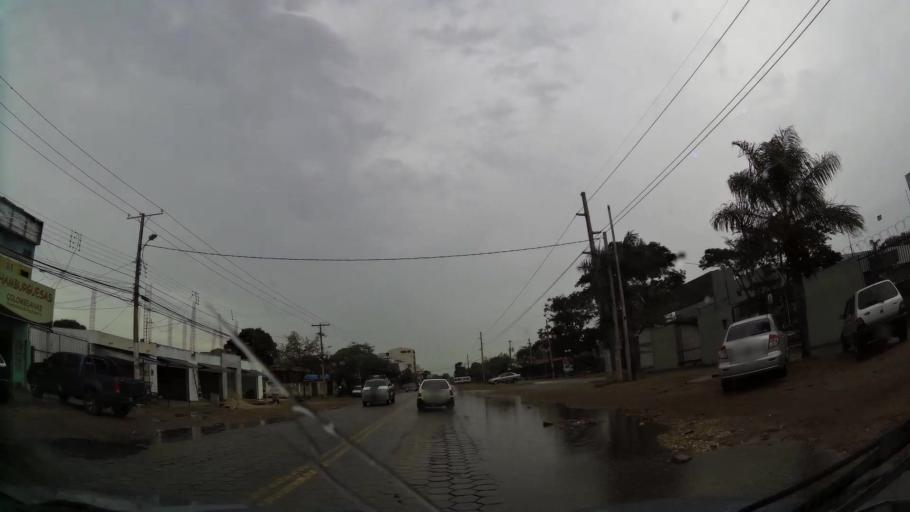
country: BO
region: Santa Cruz
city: Santa Cruz de la Sierra
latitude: -17.7709
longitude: -63.1549
